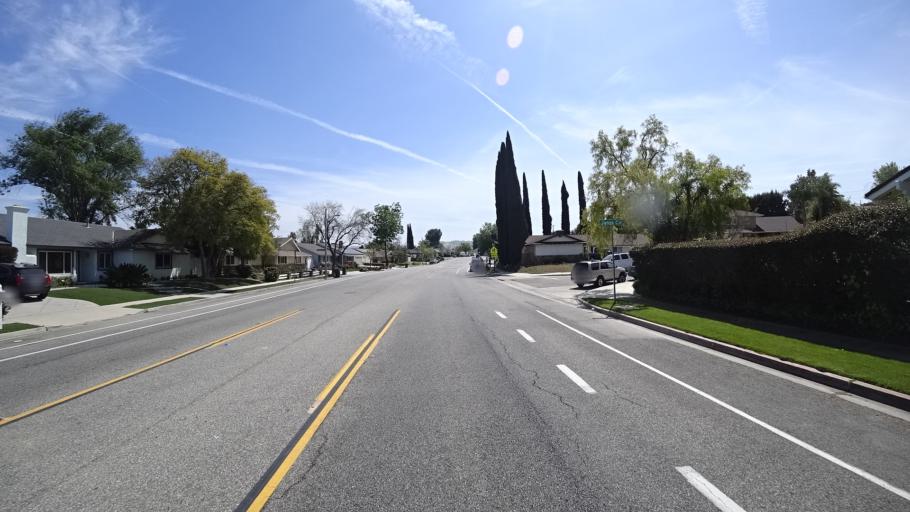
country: US
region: California
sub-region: Ventura County
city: Thousand Oaks
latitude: 34.2062
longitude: -118.8807
